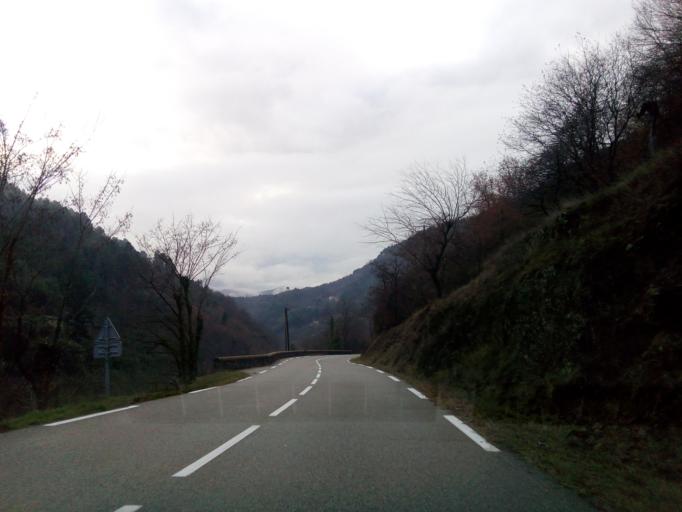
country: FR
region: Rhone-Alpes
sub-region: Departement de l'Ardeche
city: Saint-Sauveur-de-Montagut
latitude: 44.8367
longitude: 4.5777
